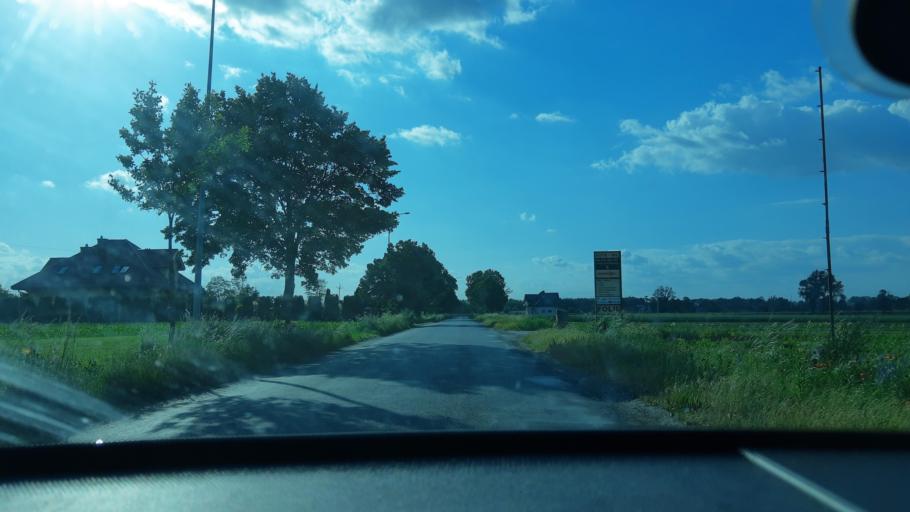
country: PL
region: Lodz Voivodeship
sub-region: Powiat sieradzki
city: Sieradz
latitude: 51.5525
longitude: 18.7661
